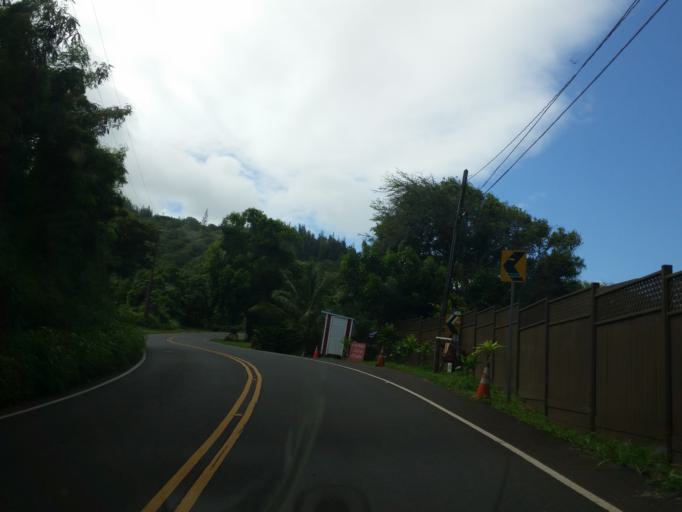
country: US
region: Hawaii
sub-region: Maui County
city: Waihee-Waiehu
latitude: 20.9467
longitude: -156.5171
